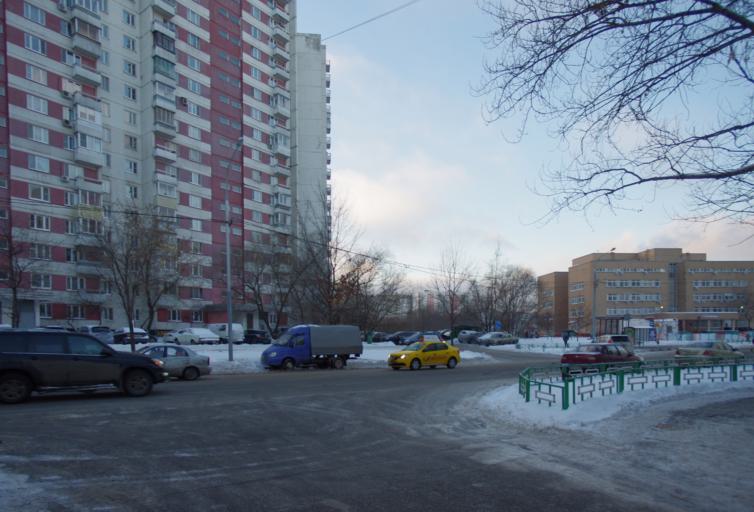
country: RU
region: Moscow
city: Orekhovo-Borisovo Severnoye
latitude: 55.6396
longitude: 37.6727
